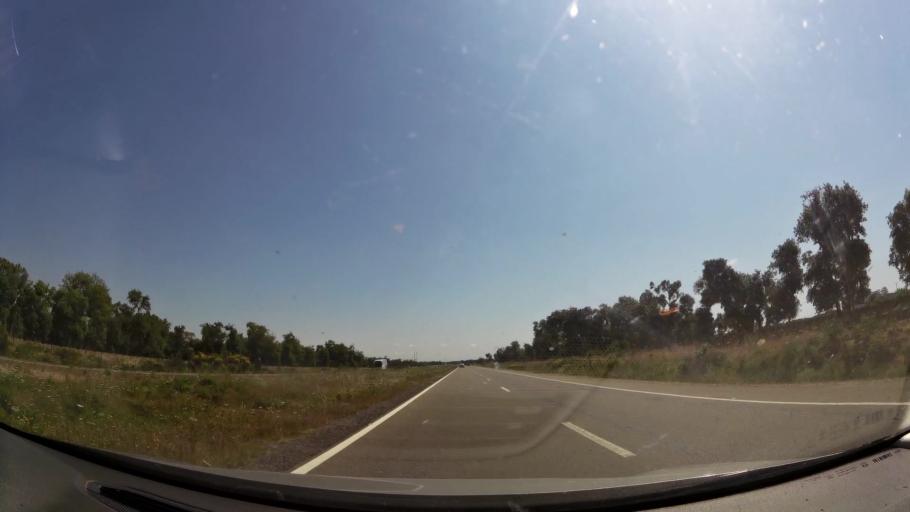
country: MA
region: Rabat-Sale-Zemmour-Zaer
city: Sale
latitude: 34.0777
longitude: -6.7006
